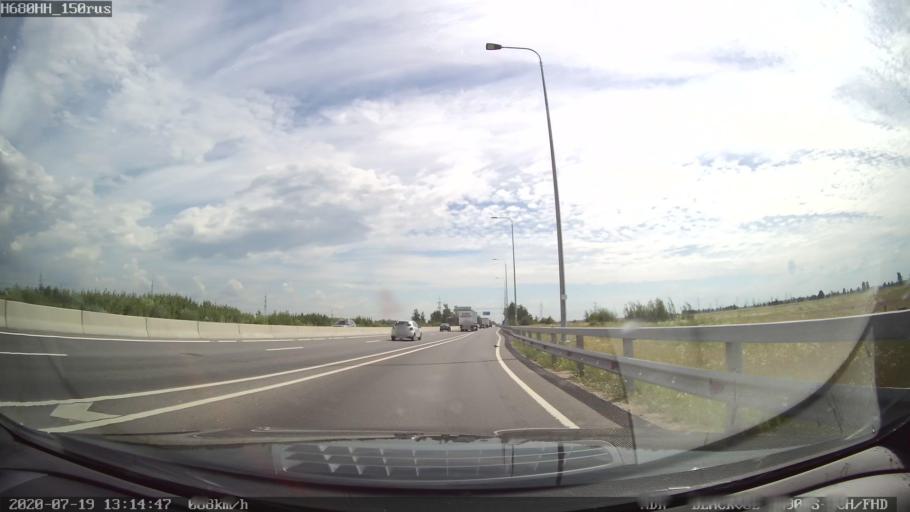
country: RU
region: St.-Petersburg
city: Kolpino
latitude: 59.7303
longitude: 30.5303
